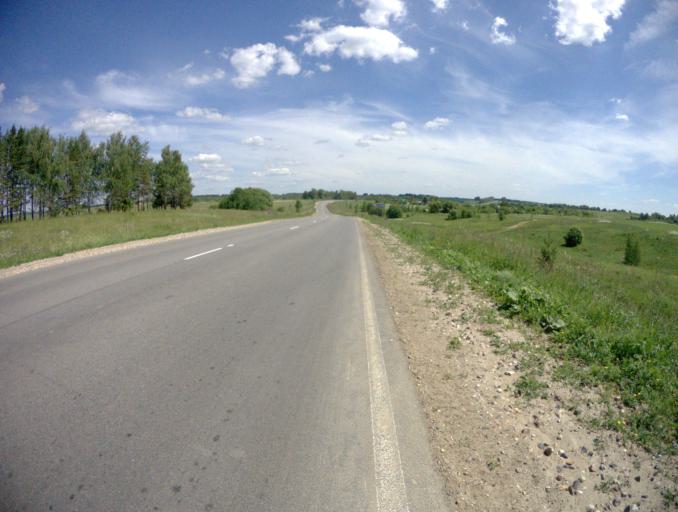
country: RU
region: Ivanovo
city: Gavrilov Posad
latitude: 56.3610
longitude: 40.0781
